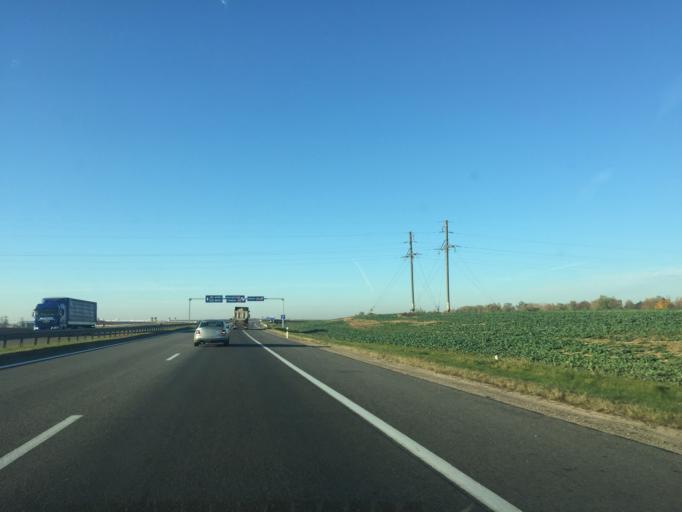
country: BY
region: Minsk
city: Pryvol'ny
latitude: 53.8091
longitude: 27.8049
